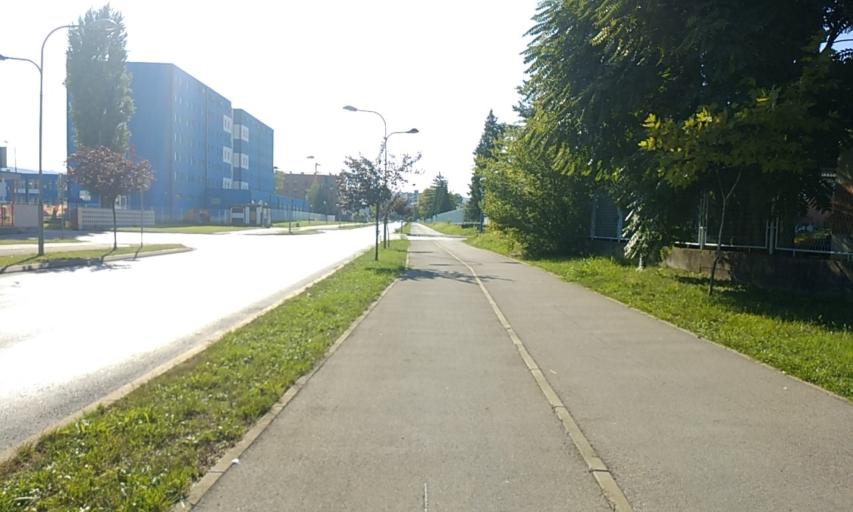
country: BA
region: Republika Srpska
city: Starcevica
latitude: 44.7729
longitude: 17.2146
